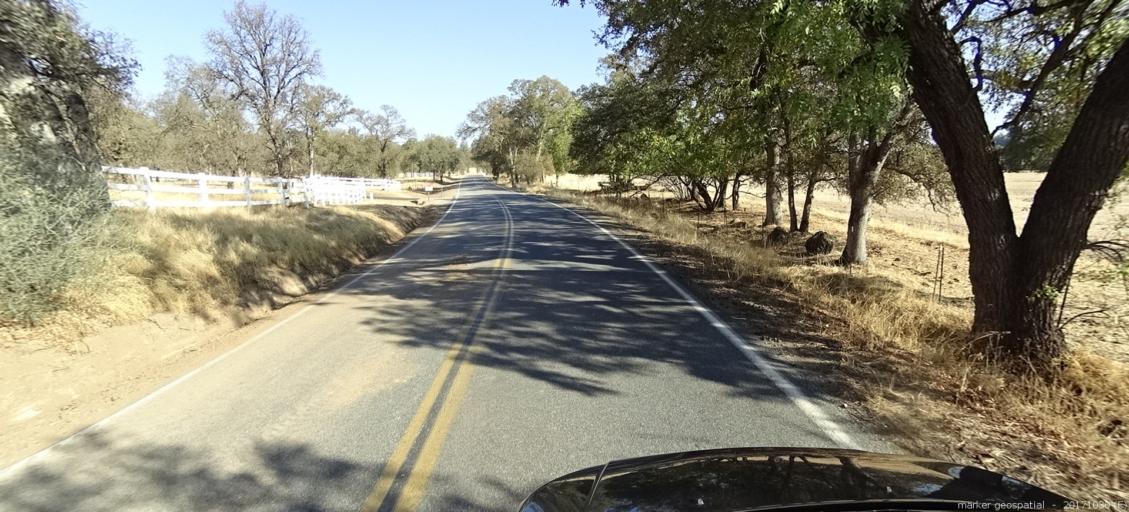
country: US
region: California
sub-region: Shasta County
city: Palo Cedro
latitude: 40.5826
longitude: -122.1792
